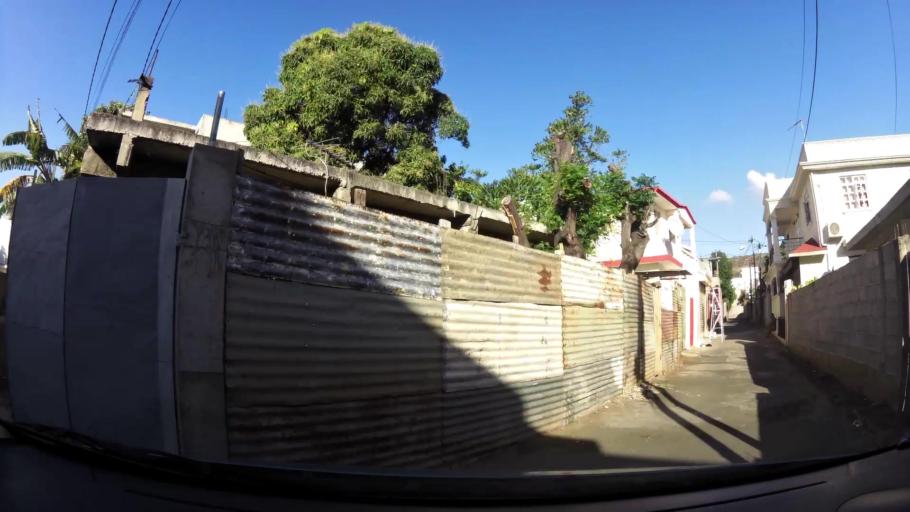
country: MU
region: Port Louis
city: Port Louis
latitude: -20.1667
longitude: 57.4812
